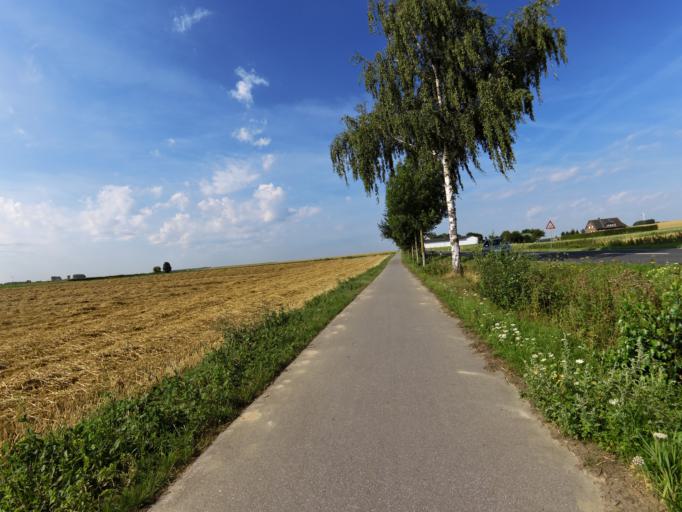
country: DE
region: North Rhine-Westphalia
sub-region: Regierungsbezirk Koln
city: Linnich
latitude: 50.9765
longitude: 6.2528
